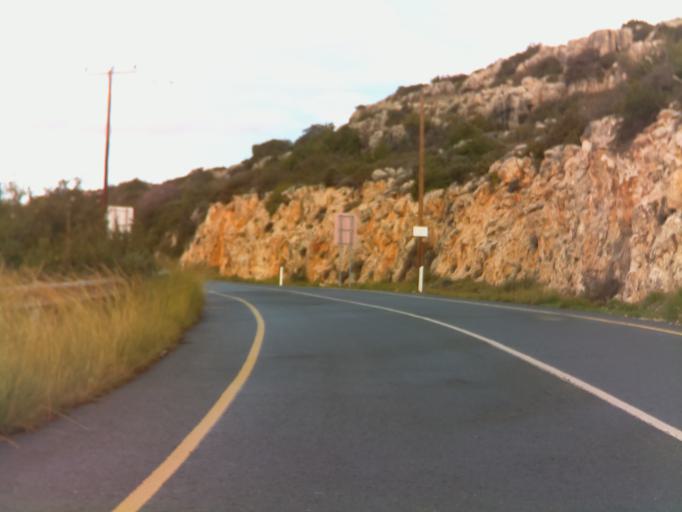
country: CY
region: Pafos
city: Pegeia
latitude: 34.8895
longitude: 32.3697
